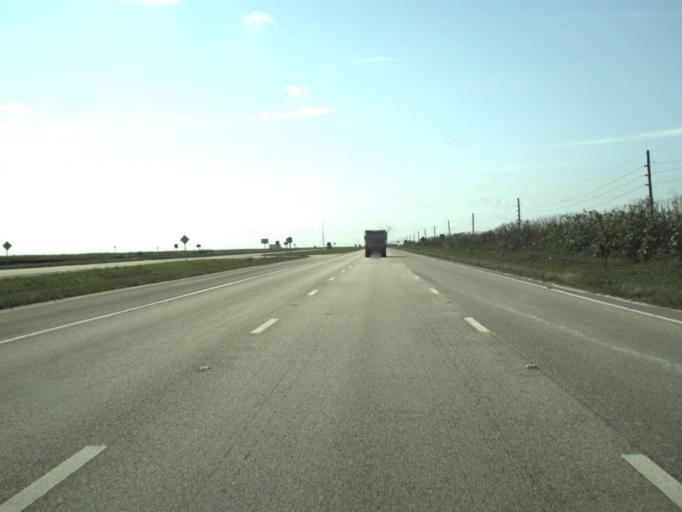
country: US
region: Florida
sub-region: Palm Beach County
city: Belle Glade Camp
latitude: 26.4578
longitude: -80.6332
